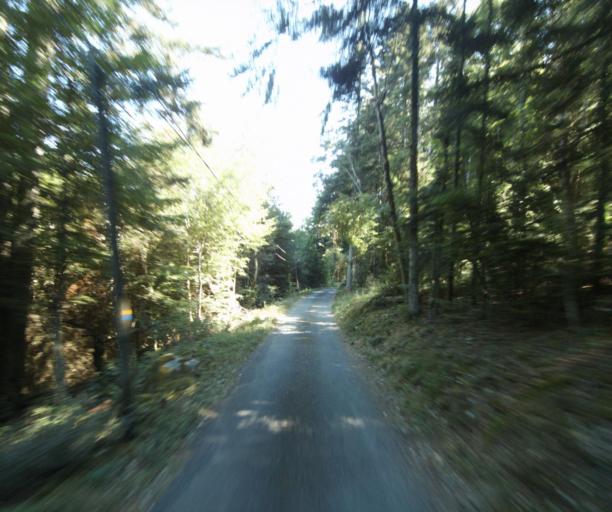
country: FR
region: Rhone-Alpes
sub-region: Departement du Rhone
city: Montrottier
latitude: 45.8088
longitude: 4.4972
